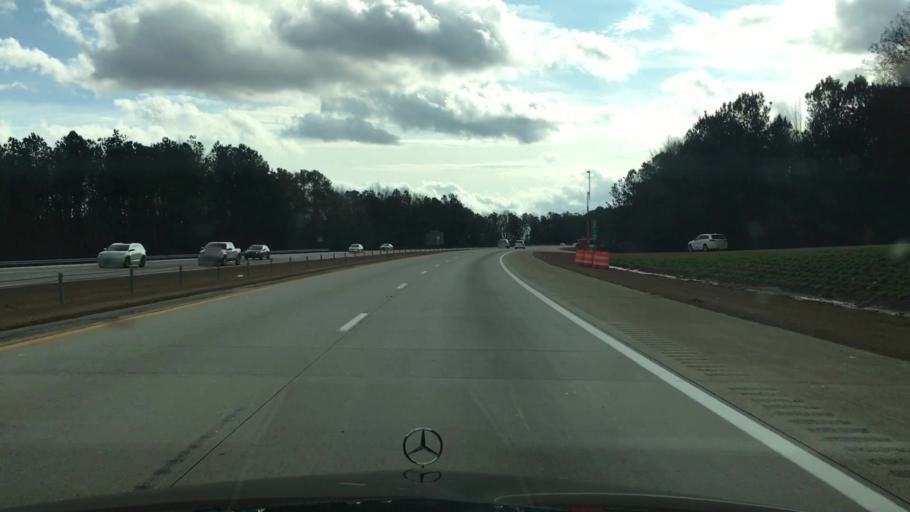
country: US
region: North Carolina
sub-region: Johnston County
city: Clayton
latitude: 35.6045
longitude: -78.5636
